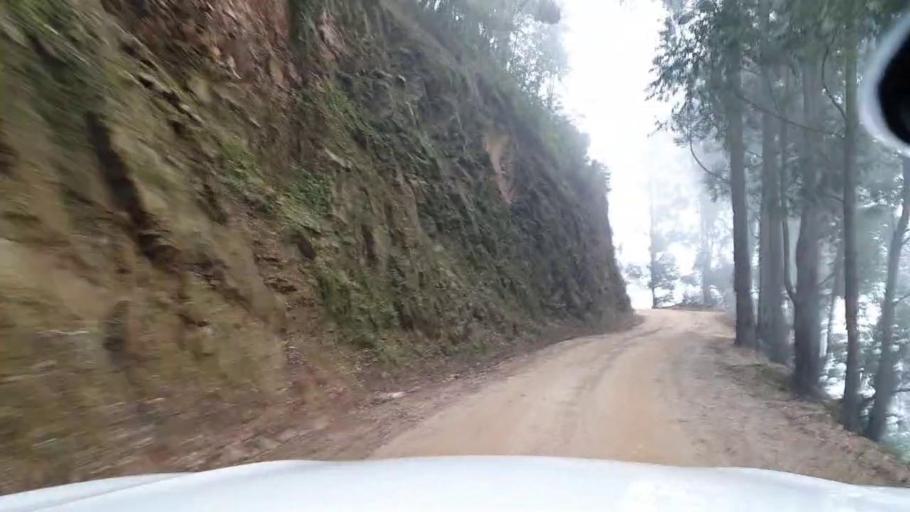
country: RW
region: Western Province
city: Cyangugu
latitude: -2.5872
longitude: 29.1877
